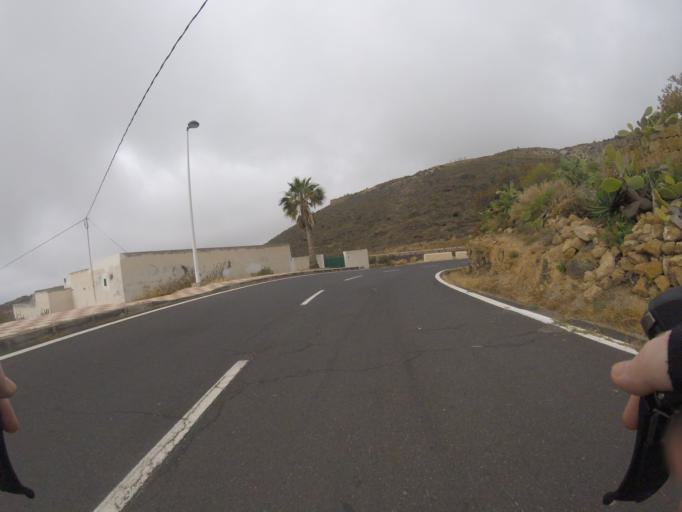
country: ES
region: Canary Islands
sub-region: Provincia de Santa Cruz de Tenerife
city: Fasnia
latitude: 28.2172
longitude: -16.4516
